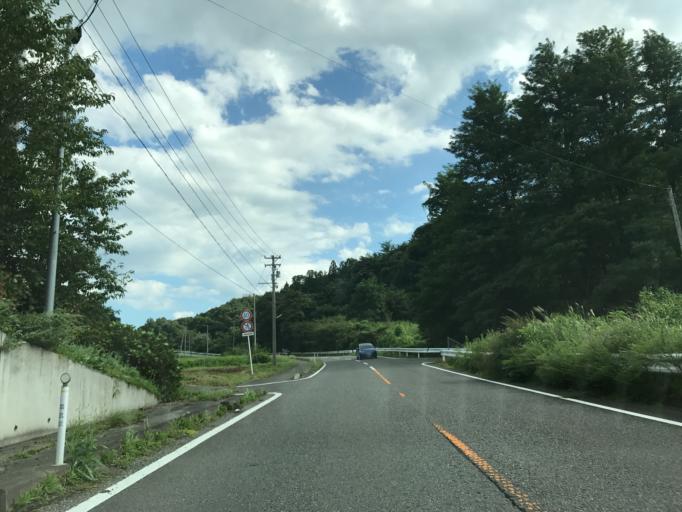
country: JP
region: Fukushima
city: Miharu
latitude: 37.4043
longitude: 140.4381
